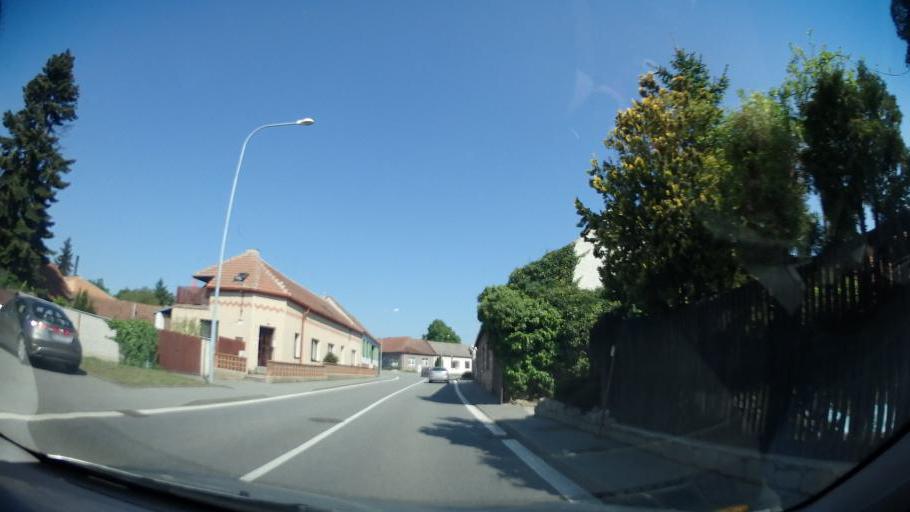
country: CZ
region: South Moravian
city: Zbraslav
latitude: 49.1817
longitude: 16.2898
